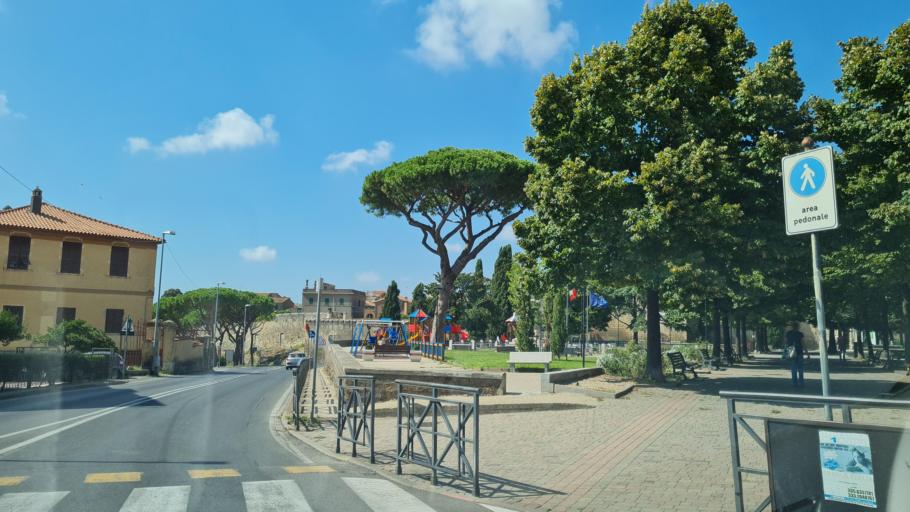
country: IT
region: Latium
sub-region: Provincia di Viterbo
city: Tarquinia
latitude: 42.2502
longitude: 11.7567
